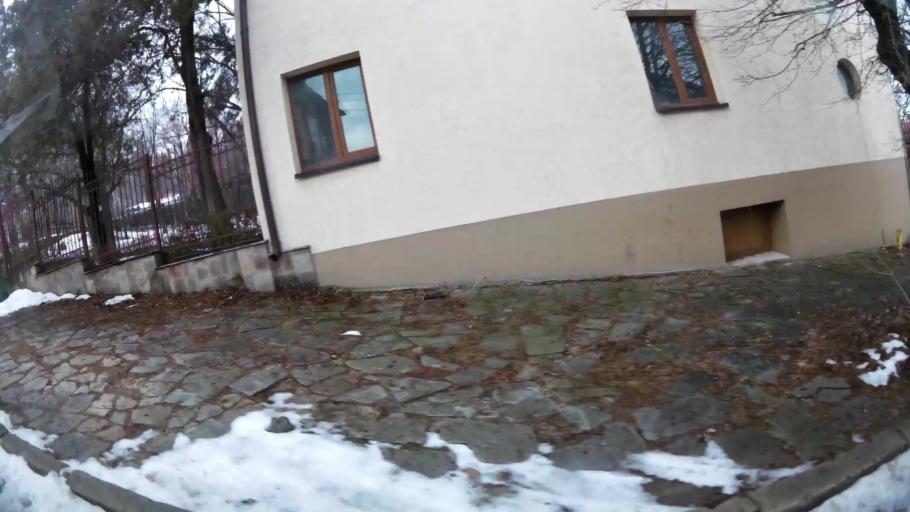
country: BG
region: Sofia-Capital
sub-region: Stolichna Obshtina
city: Sofia
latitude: 42.6462
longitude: 23.2682
